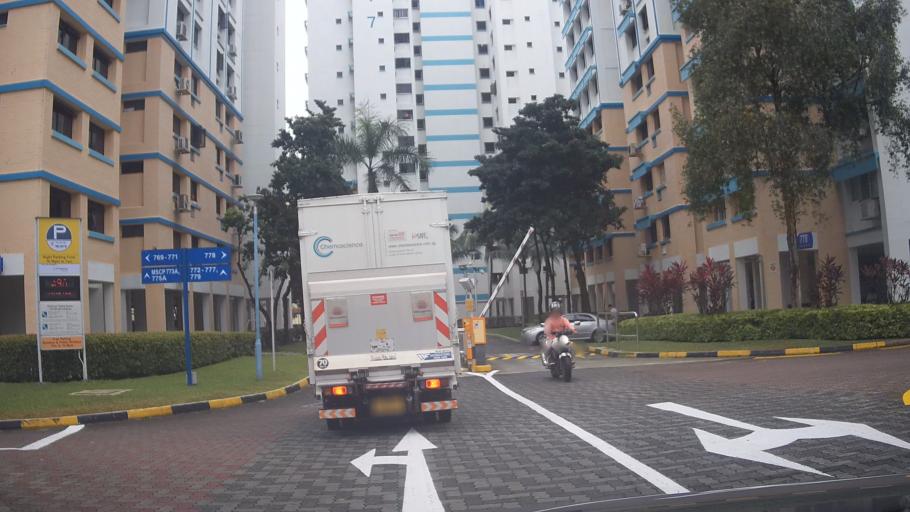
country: MY
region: Johor
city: Johor Bahru
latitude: 1.4470
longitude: 103.7994
